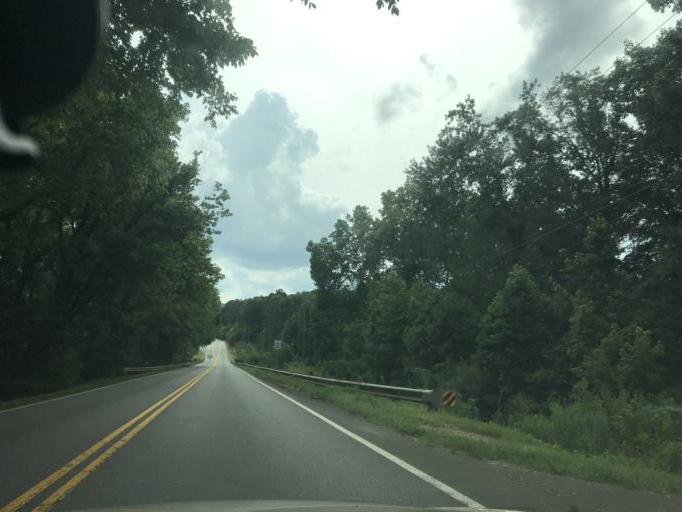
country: US
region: Georgia
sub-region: Cherokee County
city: Ball Ground
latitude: 34.2936
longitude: -84.2623
